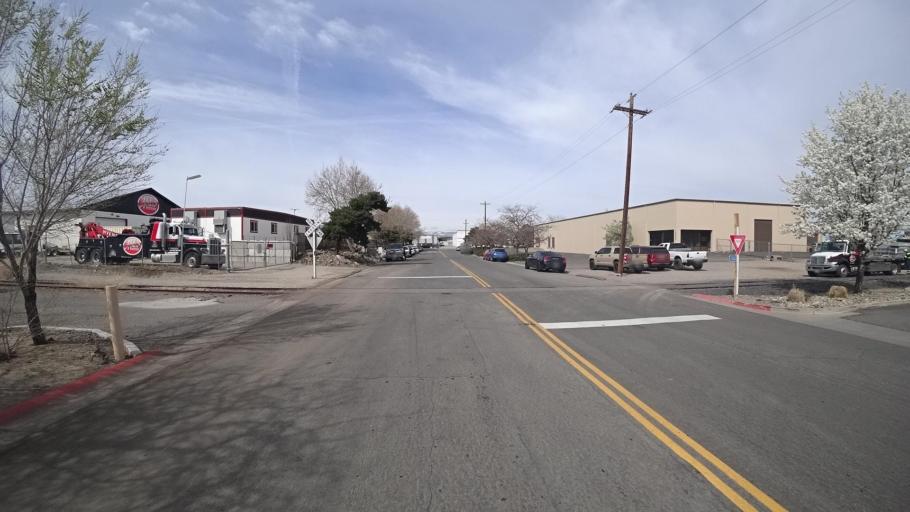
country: US
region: Nevada
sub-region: Washoe County
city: Sparks
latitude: 39.5191
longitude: -119.7525
